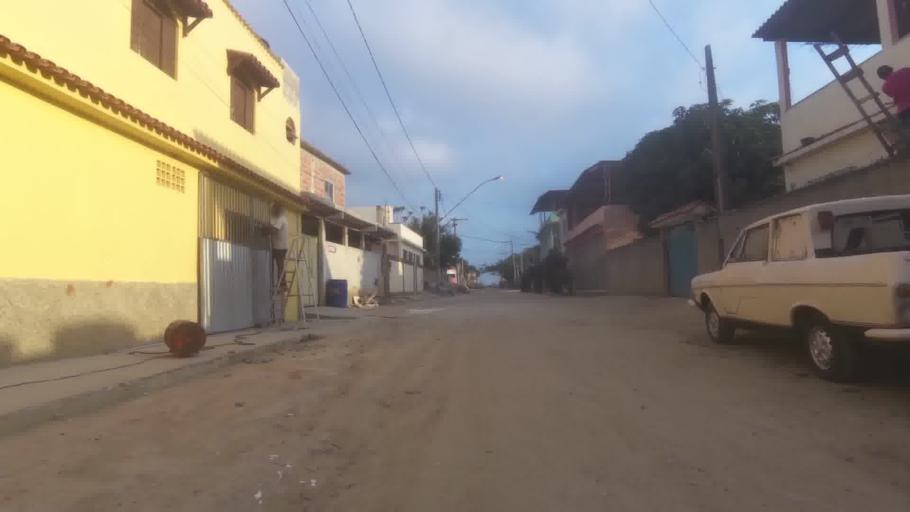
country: BR
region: Espirito Santo
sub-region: Itapemirim
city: Itapemirim
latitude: -21.0204
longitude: -40.8205
